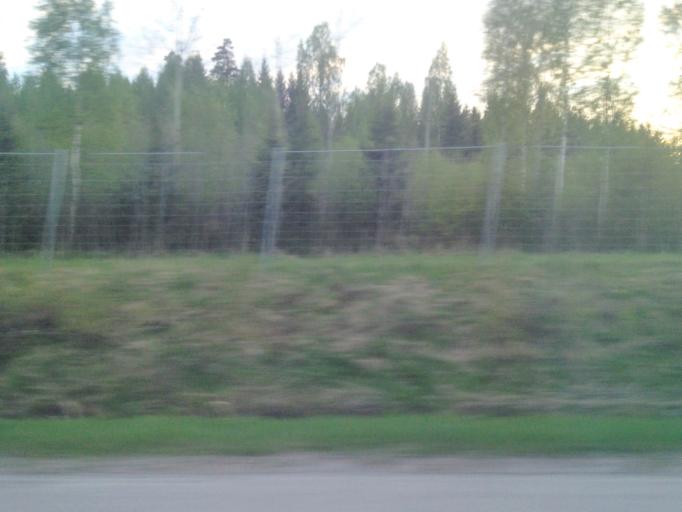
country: FI
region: Uusimaa
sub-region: Helsinki
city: Hyvinge
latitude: 60.6123
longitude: 24.8053
